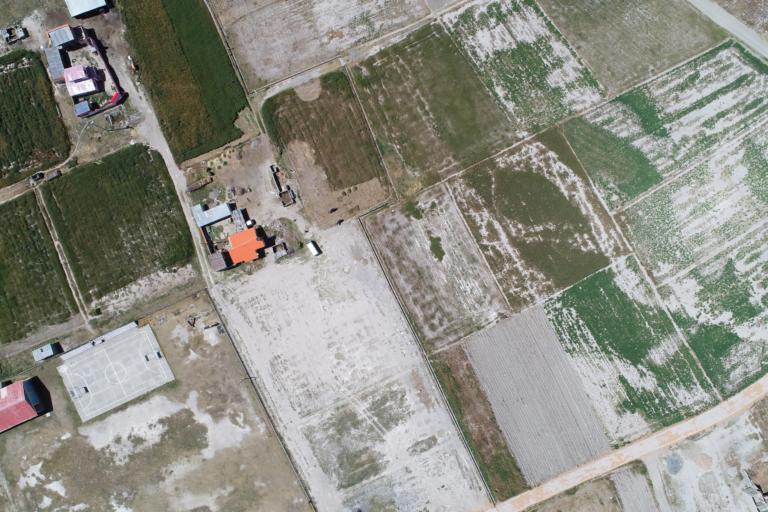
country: BO
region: La Paz
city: Achacachi
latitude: -16.0175
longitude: -68.7199
